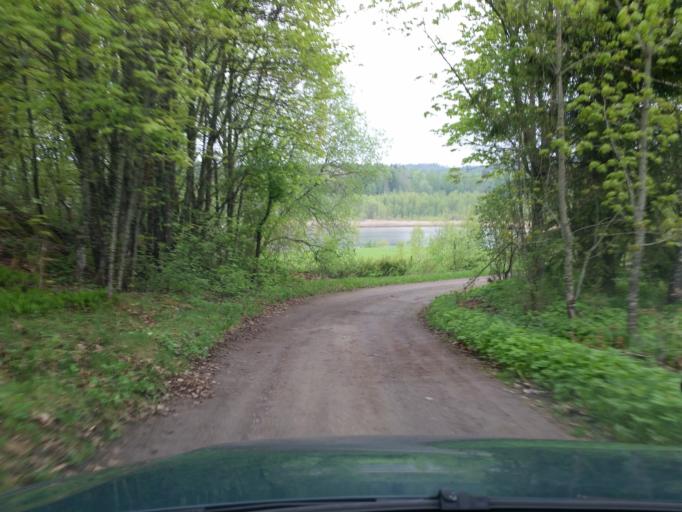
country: FI
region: Uusimaa
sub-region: Helsinki
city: Karjalohja
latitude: 60.1880
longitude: 23.6860
